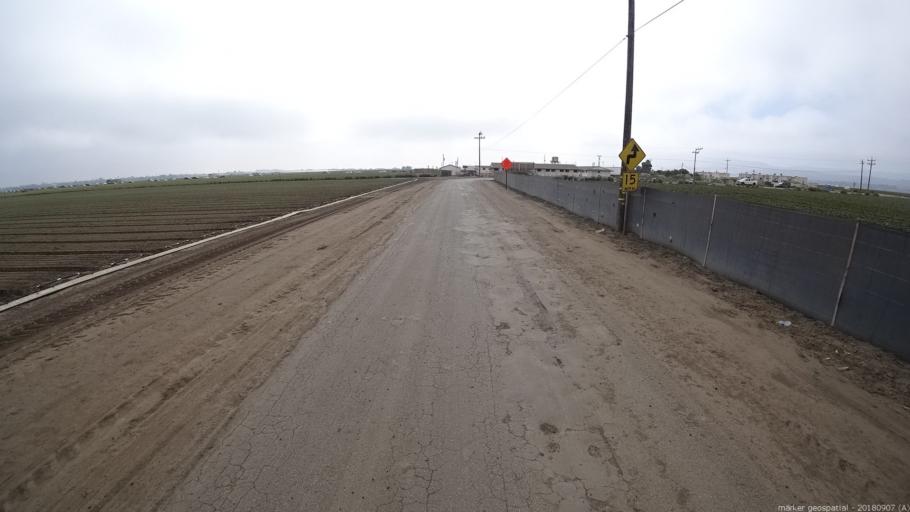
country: US
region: California
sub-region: Monterey County
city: Boronda
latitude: 36.6658
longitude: -121.7022
